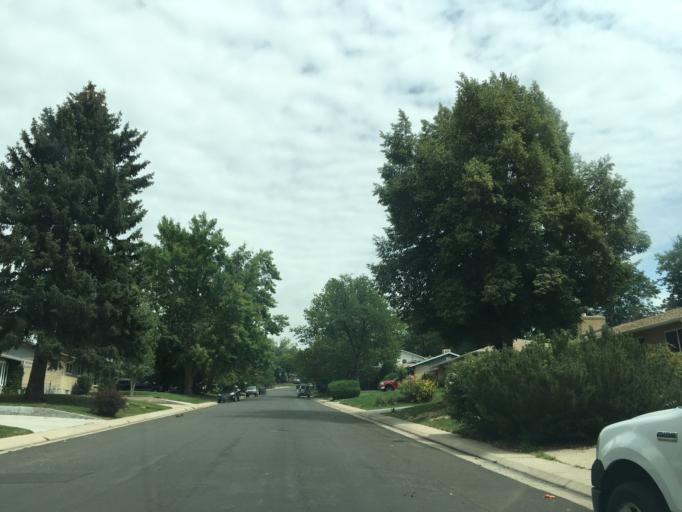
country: US
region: Colorado
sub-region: Arapahoe County
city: Sheridan
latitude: 39.6642
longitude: -105.0512
